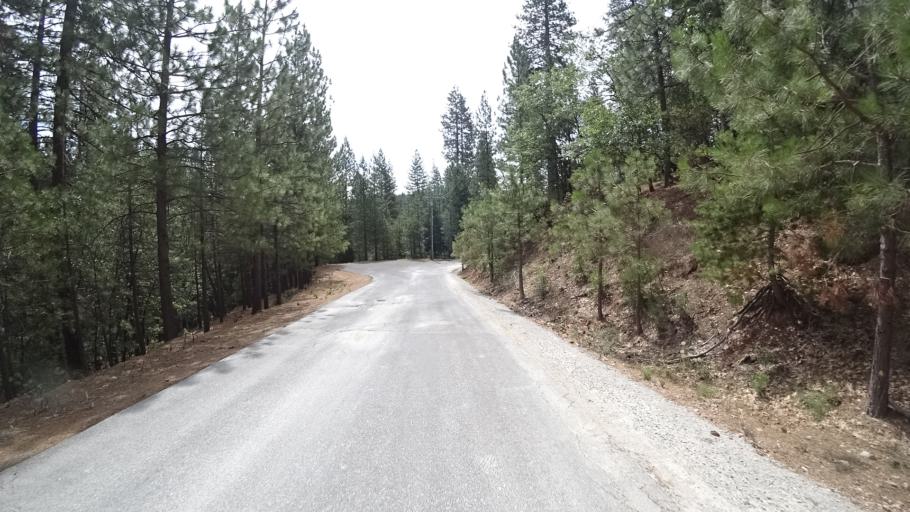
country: US
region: California
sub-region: Calaveras County
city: Arnold
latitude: 38.2437
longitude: -120.3454
